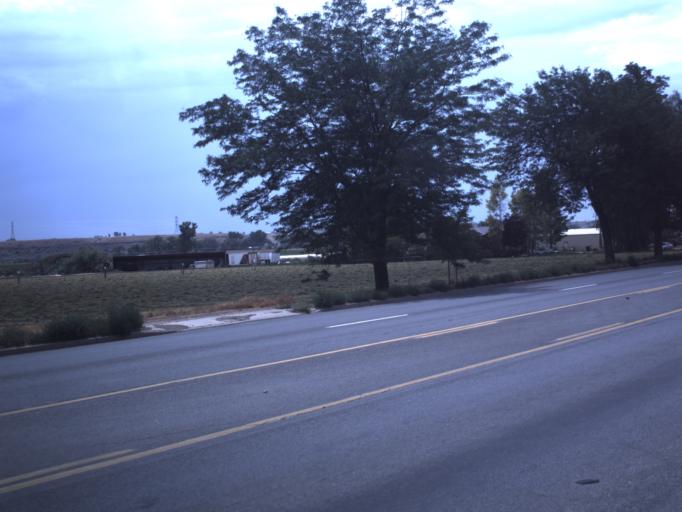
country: US
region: Utah
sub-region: Duchesne County
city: Roosevelt
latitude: 40.2857
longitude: -110.0067
